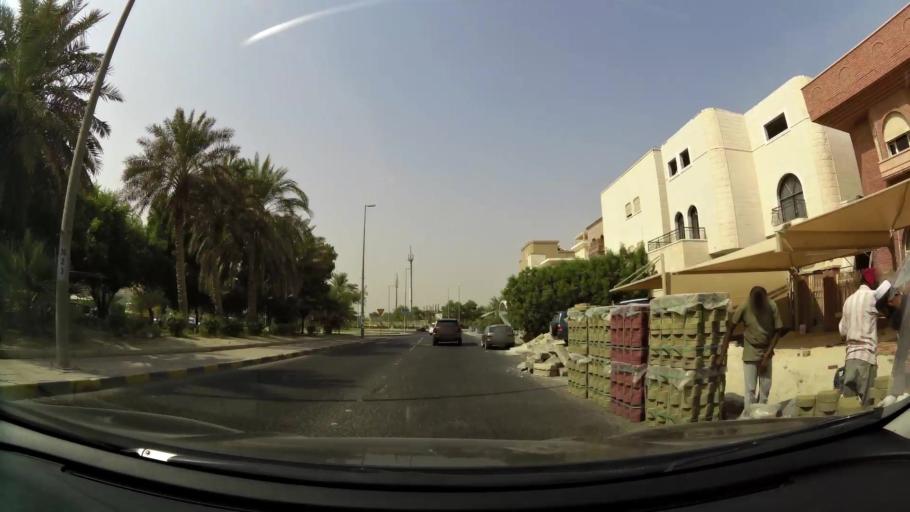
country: KW
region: Al Asimah
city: Ar Rabiyah
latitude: 29.3031
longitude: 47.8899
